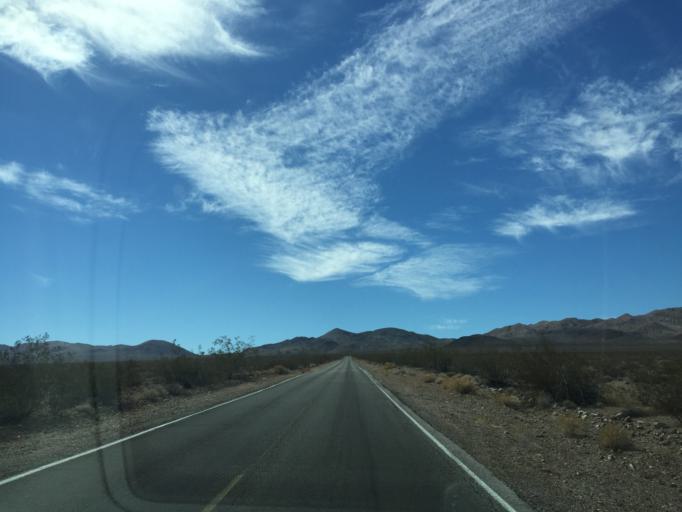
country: US
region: Nevada
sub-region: Nye County
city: Beatty
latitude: 36.2631
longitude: -116.6667
